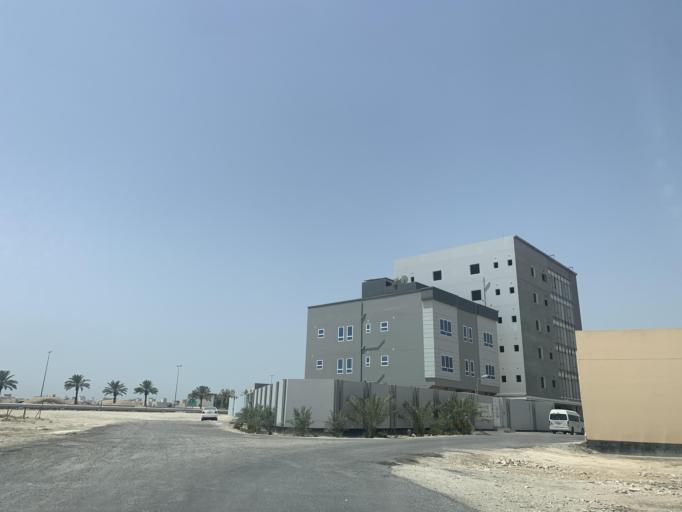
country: BH
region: Central Governorate
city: Madinat Hamad
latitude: 26.1431
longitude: 50.5039
